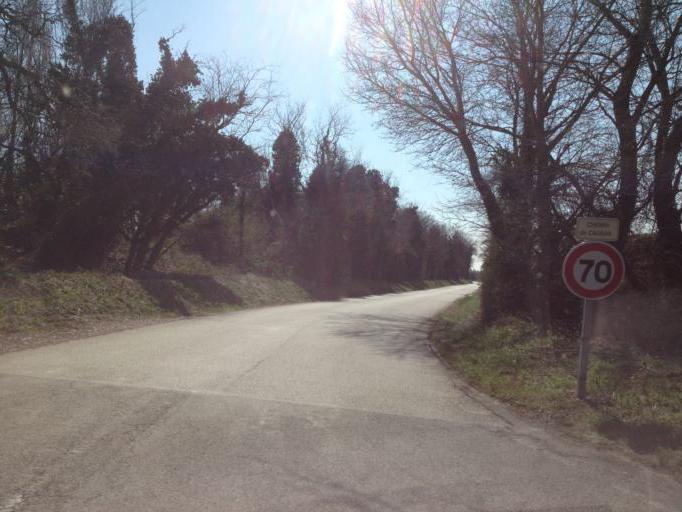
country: FR
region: Provence-Alpes-Cote d'Azur
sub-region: Departement du Vaucluse
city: Jonquieres
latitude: 44.1043
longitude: 4.9143
